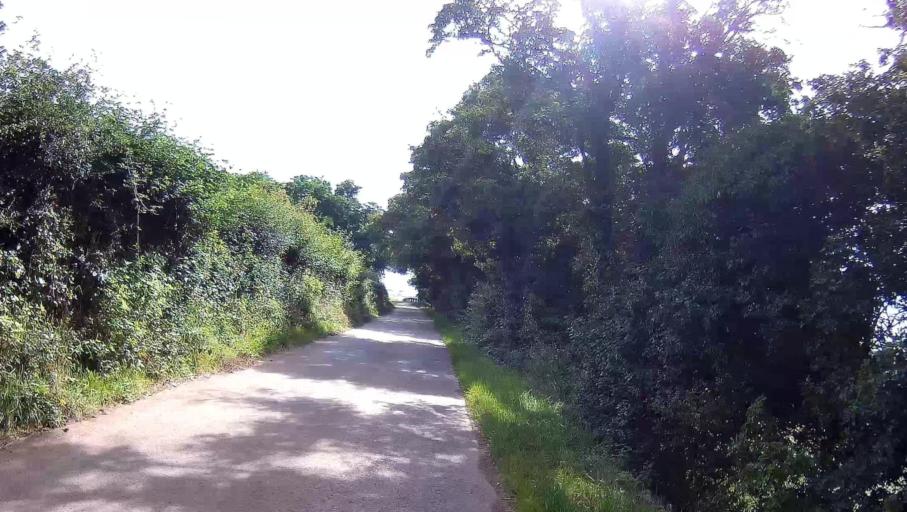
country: FR
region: Bourgogne
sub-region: Departement de Saone-et-Loire
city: Saint-Leger-sur-Dheune
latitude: 46.8675
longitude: 4.6312
